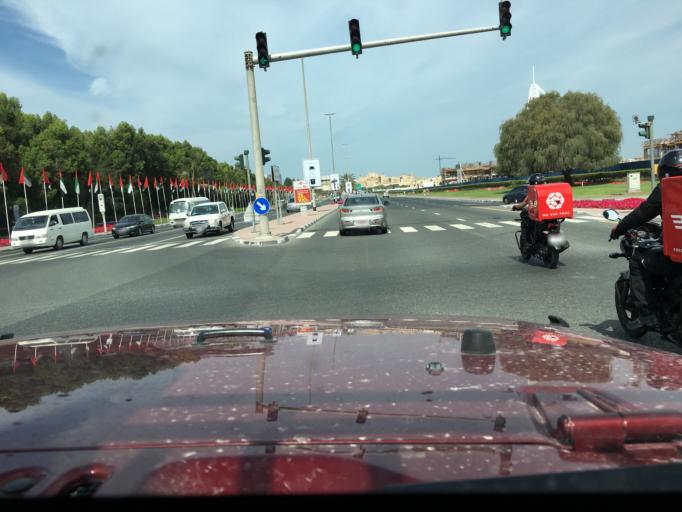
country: AE
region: Dubai
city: Dubai
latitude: 25.1280
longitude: 55.1950
